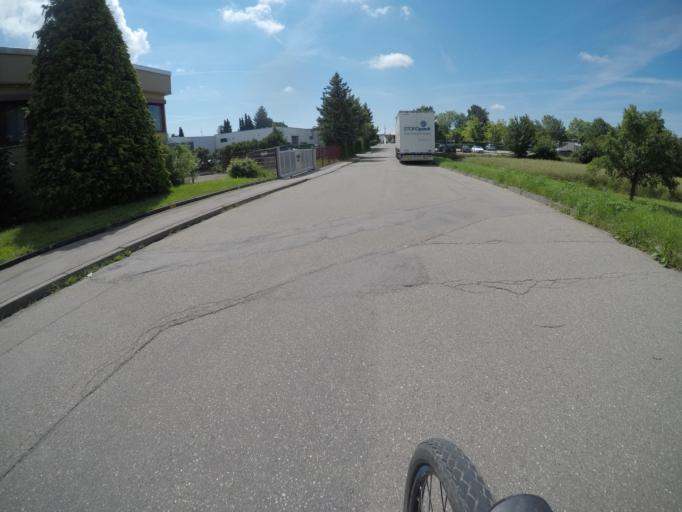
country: DE
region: Baden-Wuerttemberg
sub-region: Regierungsbezirk Stuttgart
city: Deckenpfronn
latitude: 48.6233
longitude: 8.8285
